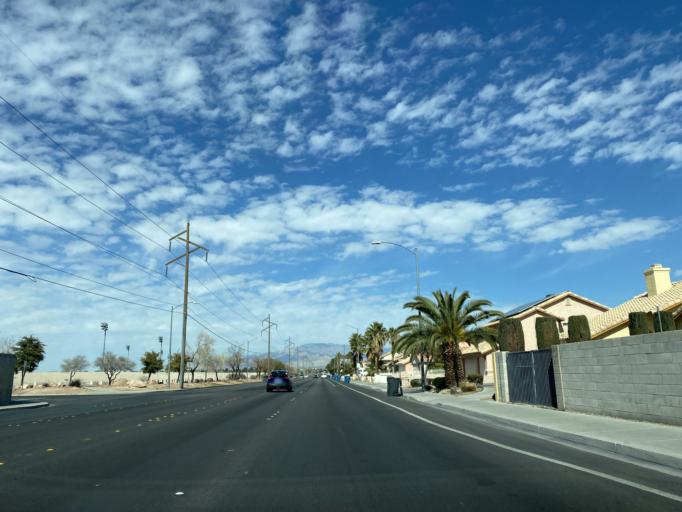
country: US
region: Nevada
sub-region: Clark County
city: Spring Valley
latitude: 36.2214
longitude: -115.2513
